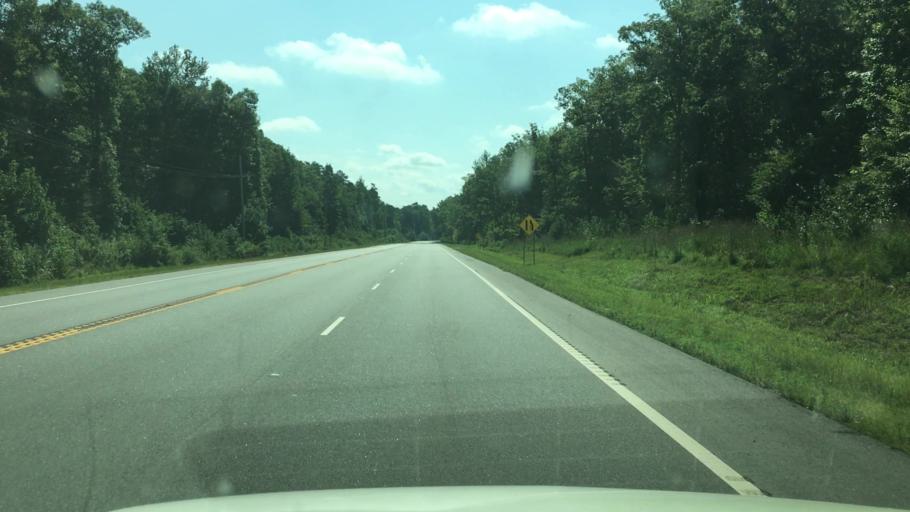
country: US
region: Arkansas
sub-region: Garland County
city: Rockwell
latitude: 34.5179
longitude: -93.3084
